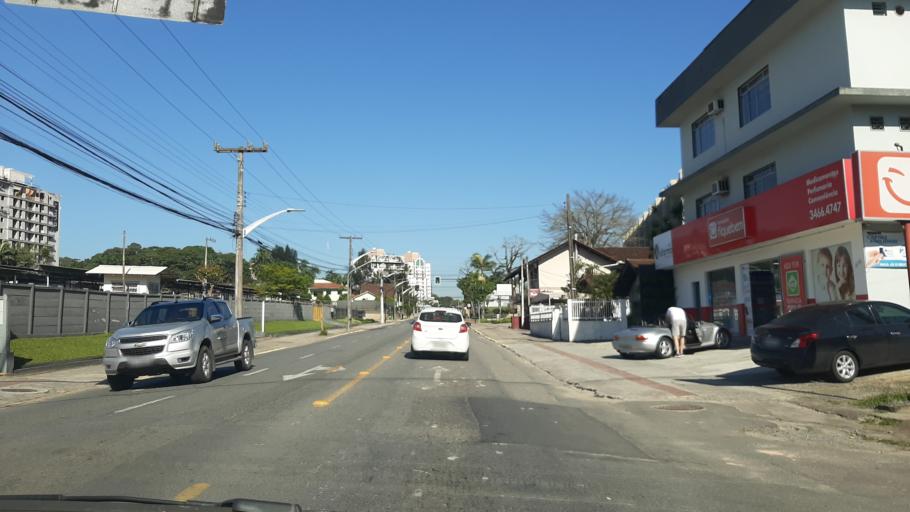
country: BR
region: Santa Catarina
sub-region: Joinville
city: Joinville
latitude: -26.3152
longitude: -48.8620
